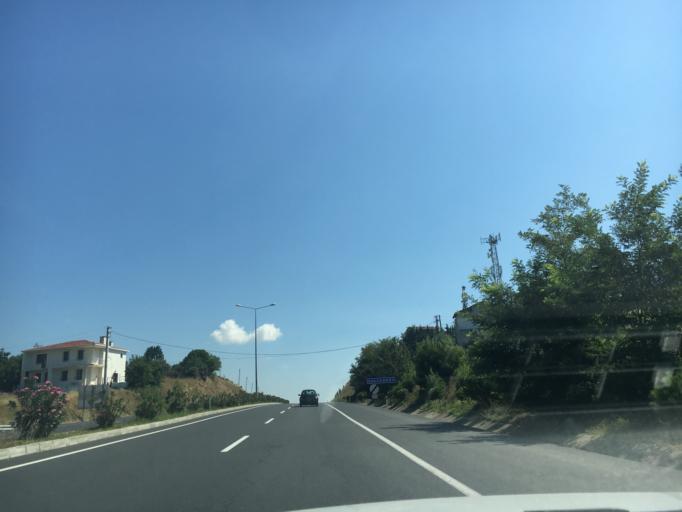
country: TR
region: Tekirdag
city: Sultankoy
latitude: 41.0219
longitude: 27.9942
